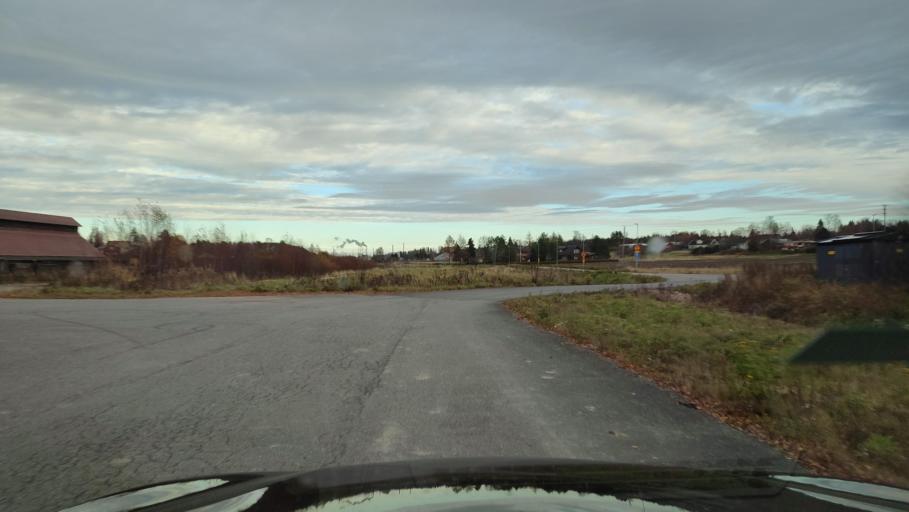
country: FI
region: Ostrobothnia
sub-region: Sydosterbotten
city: Naerpes
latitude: 62.4664
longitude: 21.3614
